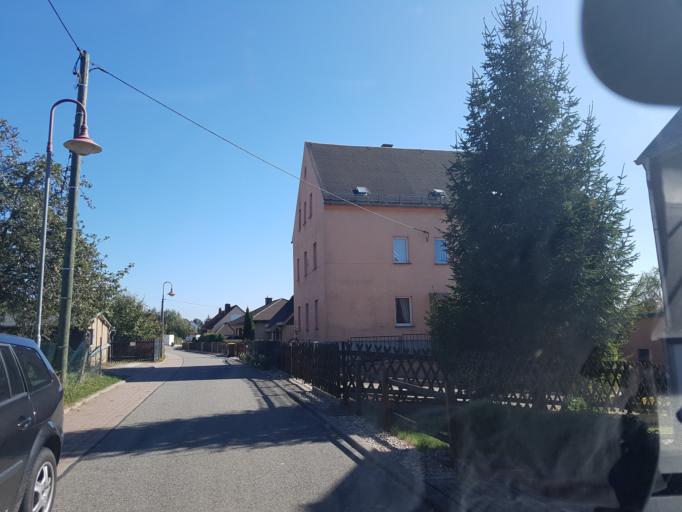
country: DE
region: Saxony
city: Waldheim
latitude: 51.0784
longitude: 12.9992
